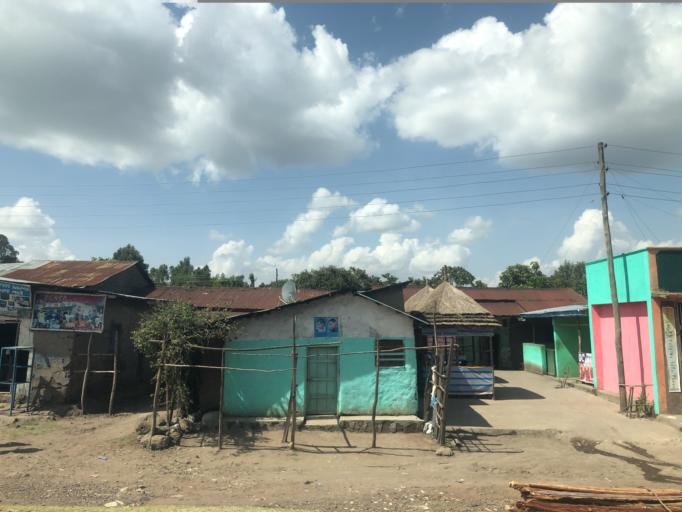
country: ET
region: Southern Nations, Nationalities, and People's Region
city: Boditi
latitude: 7.0333
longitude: 37.9200
